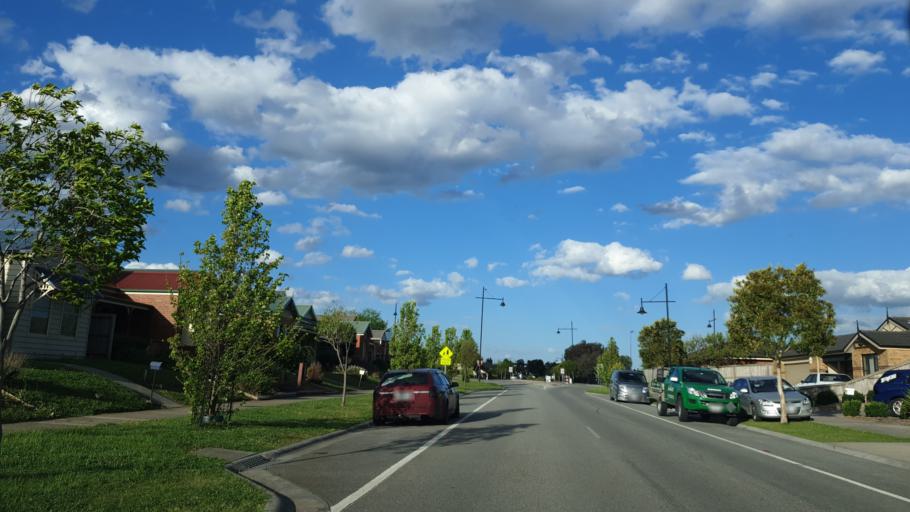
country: AU
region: Victoria
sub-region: Casey
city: Cranbourne North
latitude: -38.0870
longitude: 145.2868
